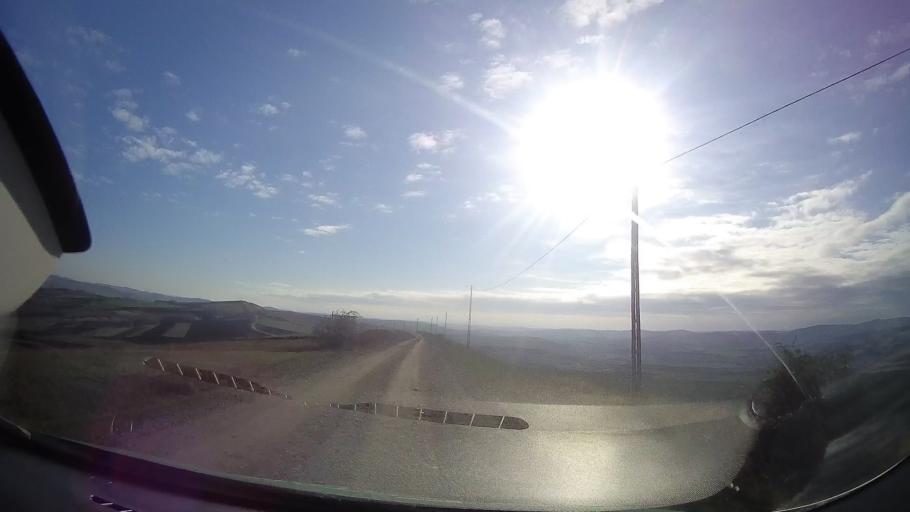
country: RO
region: Mures
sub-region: Comuna Saulia
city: Saulia
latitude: 46.5893
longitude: 24.2217
